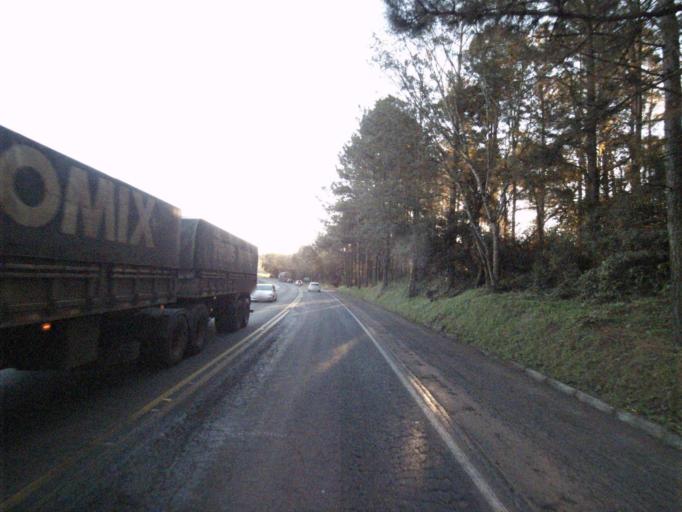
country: BR
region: Santa Catarina
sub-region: Sao Lourenco Do Oeste
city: Sao Lourenco dOeste
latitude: -26.8257
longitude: -53.0854
